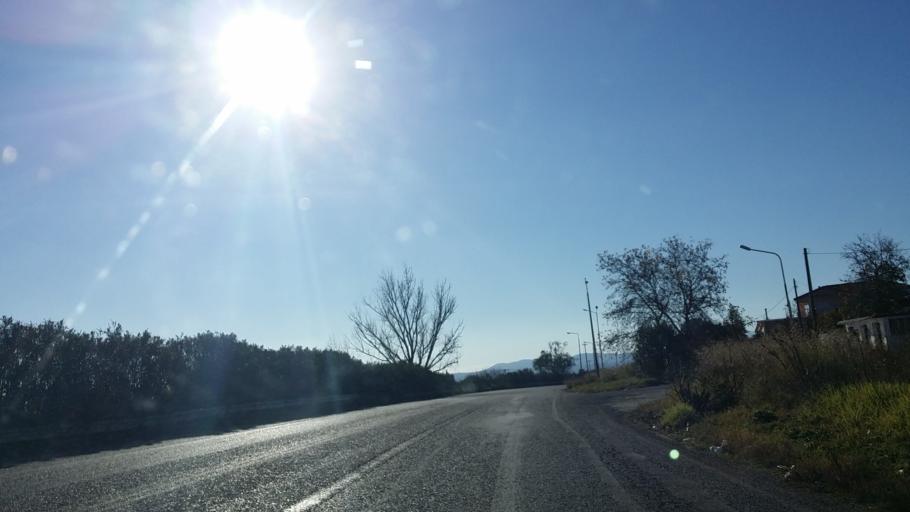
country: GR
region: West Greece
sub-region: Nomos Aitolias kai Akarnanias
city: Neapolis
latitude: 38.6685
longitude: 21.3226
